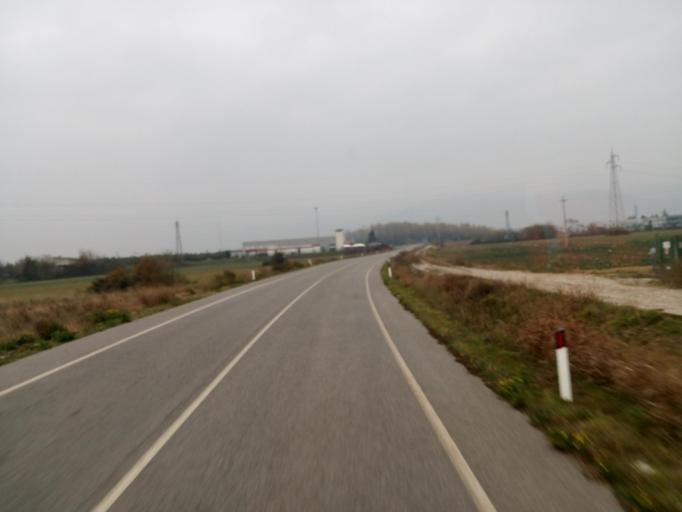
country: IT
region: Friuli Venezia Giulia
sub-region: Provincia di Udine
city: Premariacco
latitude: 46.0776
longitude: 13.3853
